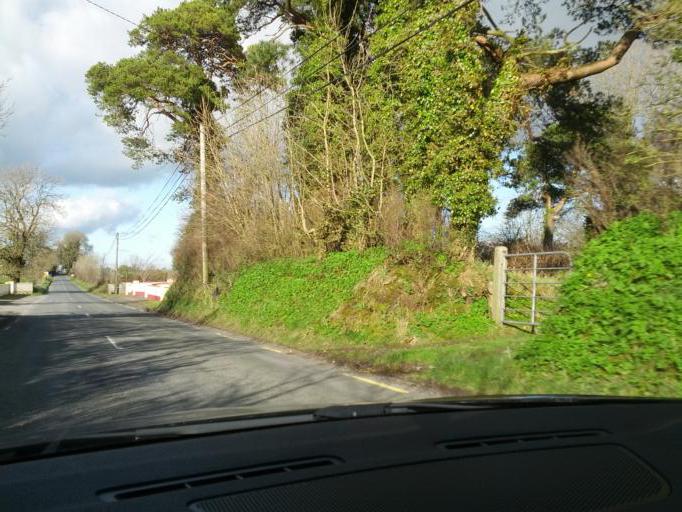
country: IE
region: Connaught
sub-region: Roscommon
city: Castlerea
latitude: 53.6729
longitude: -8.4956
